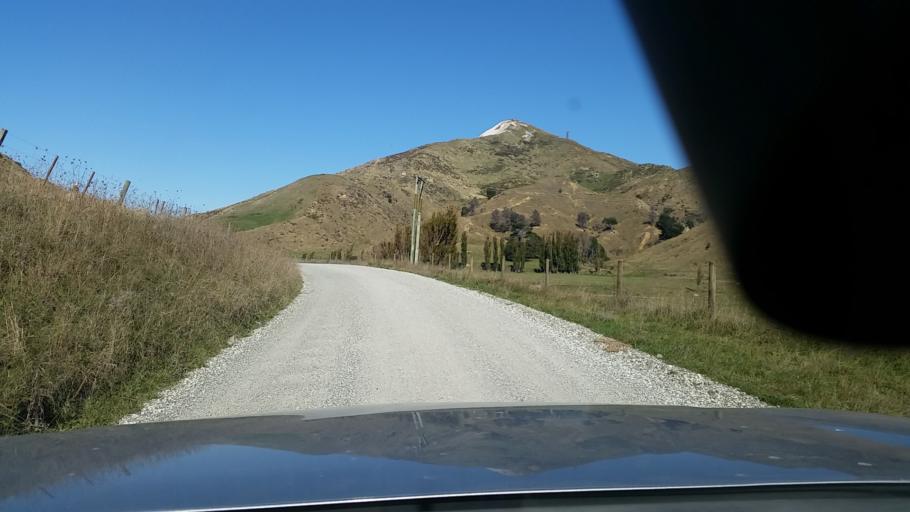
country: NZ
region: Marlborough
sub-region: Marlborough District
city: Blenheim
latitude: -41.8323
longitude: 174.1750
